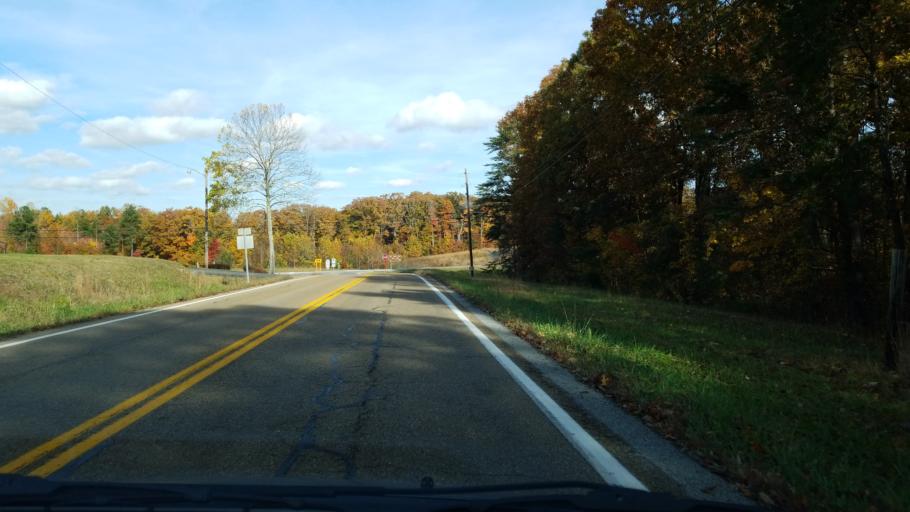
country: US
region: Tennessee
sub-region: Sequatchie County
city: Dunlap
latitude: 35.4743
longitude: -85.4623
